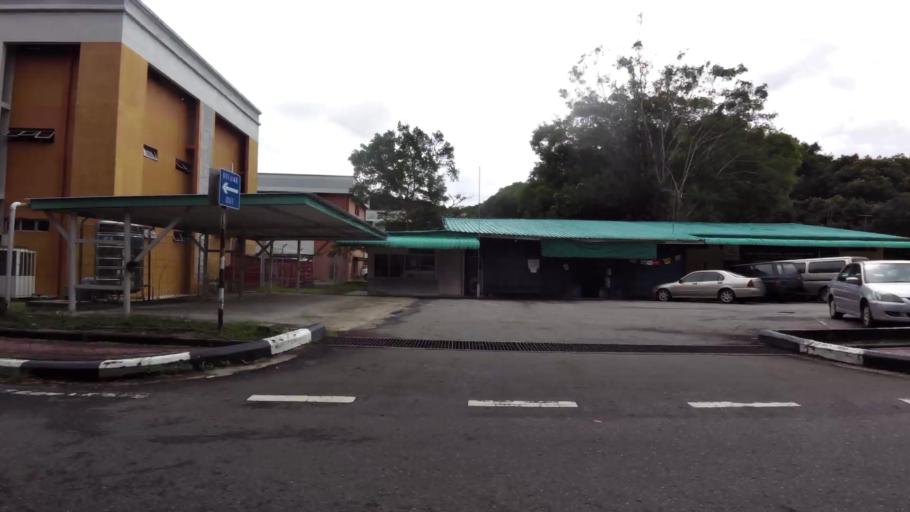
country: BN
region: Brunei and Muara
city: Bandar Seri Begawan
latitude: 4.8997
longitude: 114.9408
